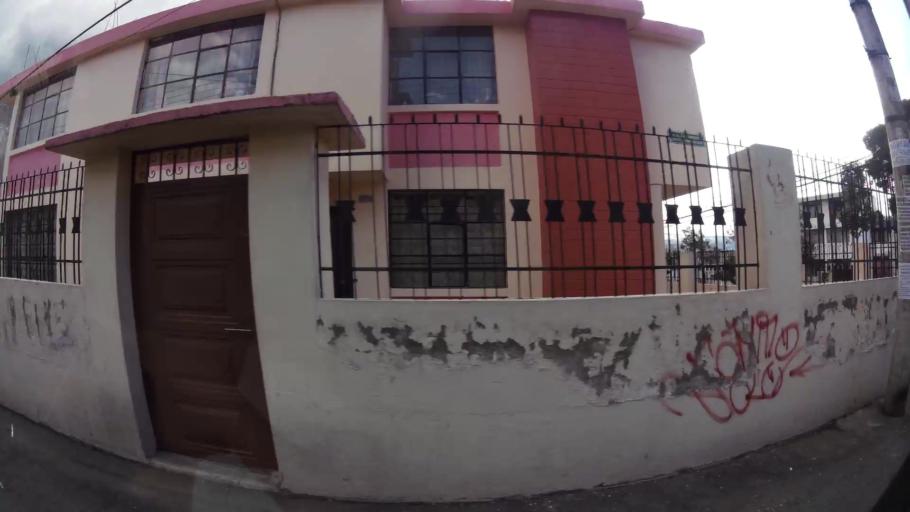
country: EC
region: Pichincha
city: Quito
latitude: -0.1237
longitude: -78.4869
